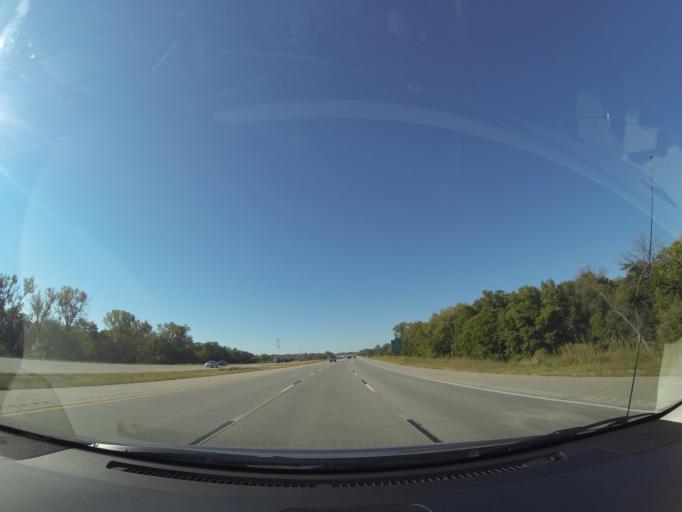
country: US
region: Nebraska
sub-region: Saunders County
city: Ashland
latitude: 41.0311
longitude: -96.2932
